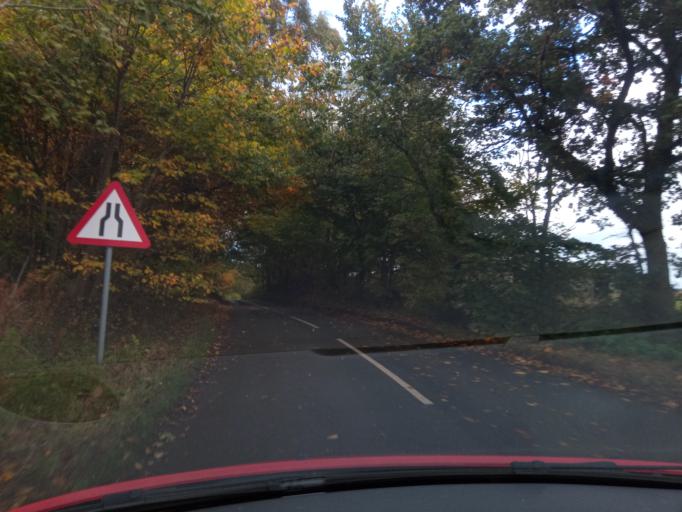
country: GB
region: Scotland
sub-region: The Scottish Borders
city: Newtown St Boswells
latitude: 55.5531
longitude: -2.7048
